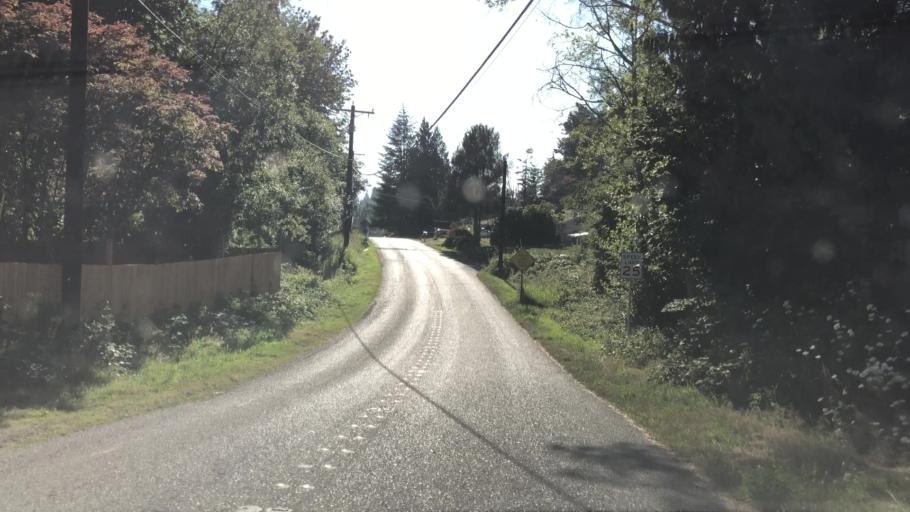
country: US
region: Washington
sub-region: Snohomish County
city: Martha Lake
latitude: 47.8449
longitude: -122.2515
